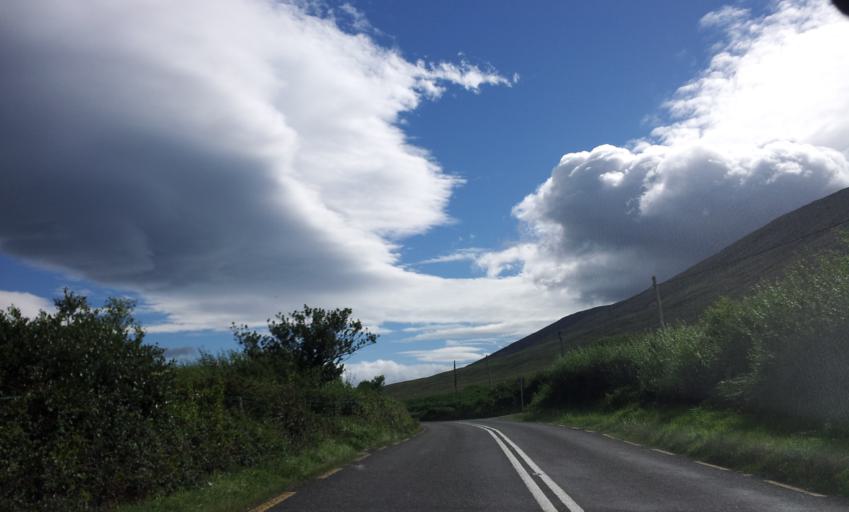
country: IE
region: Munster
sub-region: Ciarrai
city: Killorglin
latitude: 52.2311
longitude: -9.8706
